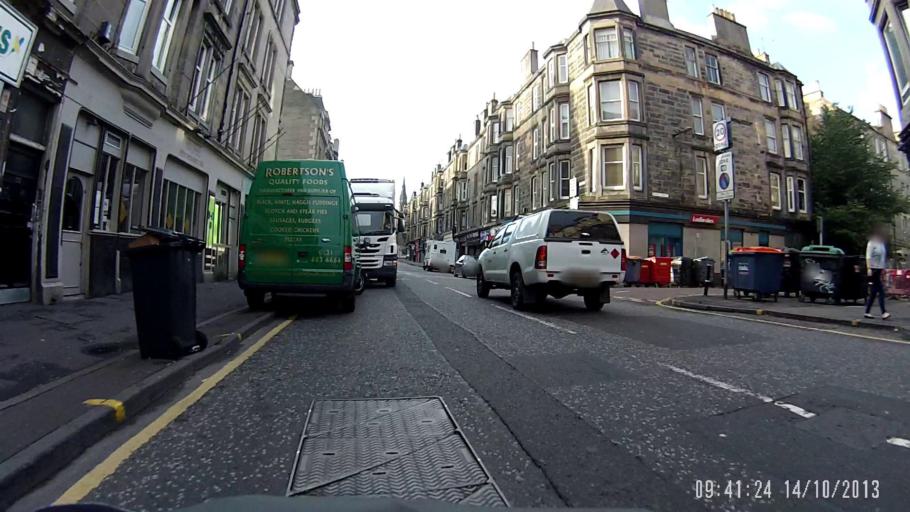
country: GB
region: Scotland
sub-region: West Lothian
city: Seafield
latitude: 55.9597
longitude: -3.1716
